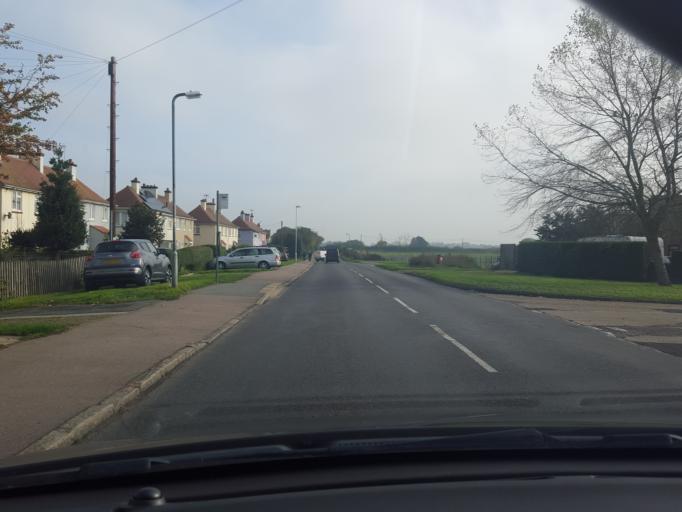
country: GB
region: England
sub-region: Essex
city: Mistley
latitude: 51.9406
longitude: 1.0906
